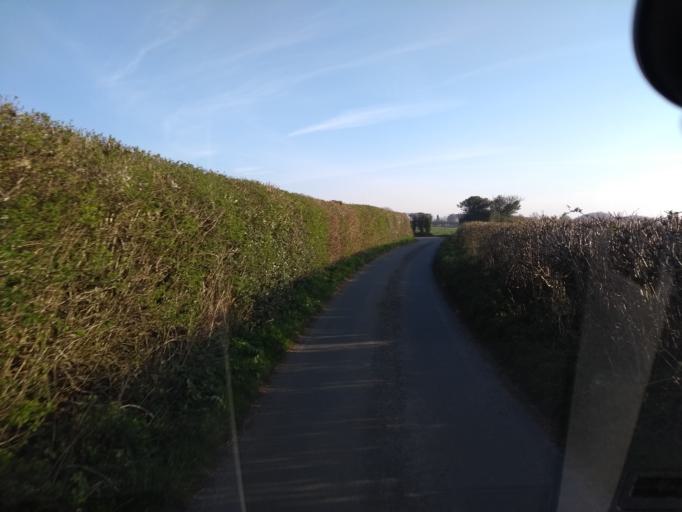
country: GB
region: England
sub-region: Somerset
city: Crewkerne
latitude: 50.8574
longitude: -2.8140
